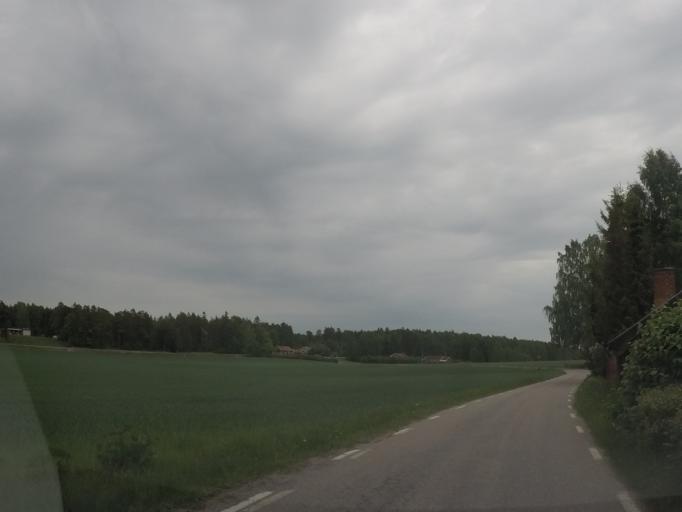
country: SE
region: Soedermanland
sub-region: Nykopings Kommun
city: Stigtomta
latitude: 58.8664
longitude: 16.8967
